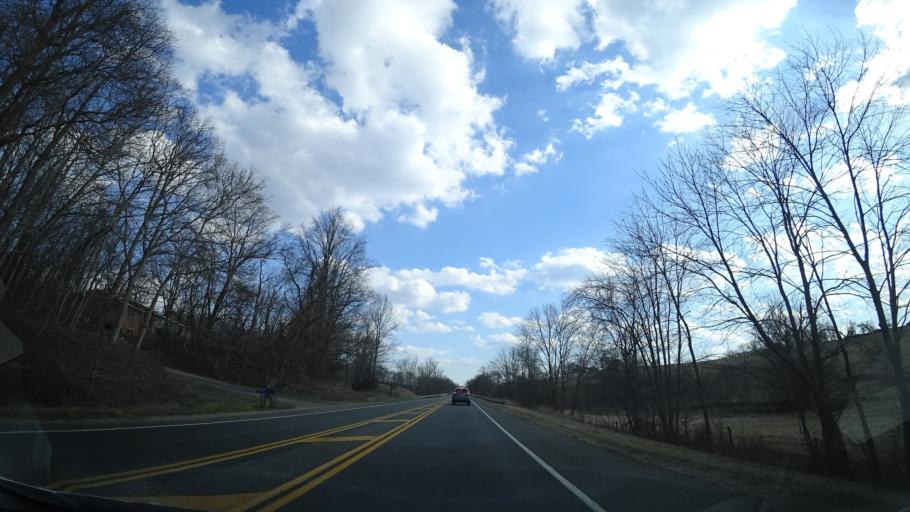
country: US
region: Virginia
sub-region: Fauquier County
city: Marshall
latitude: 38.9356
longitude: -77.9338
